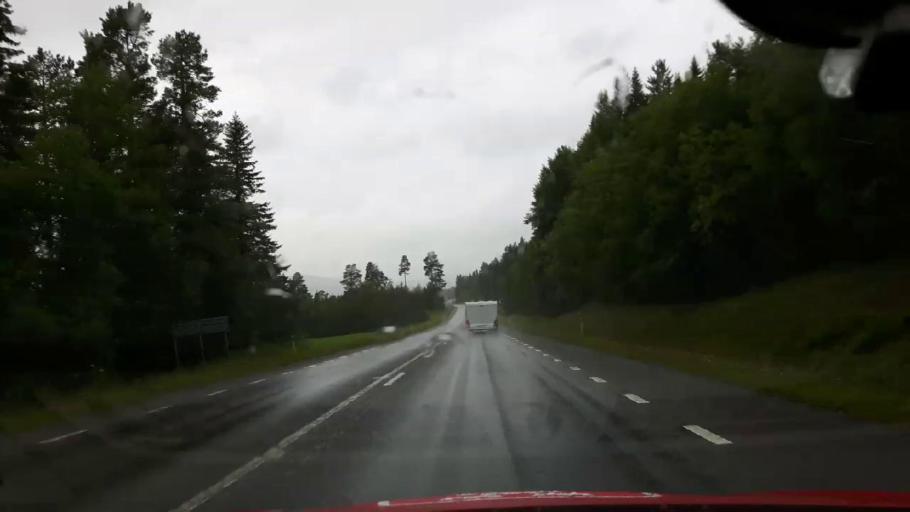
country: SE
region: Jaemtland
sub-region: Are Kommun
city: Jarpen
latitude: 63.3383
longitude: 13.4971
